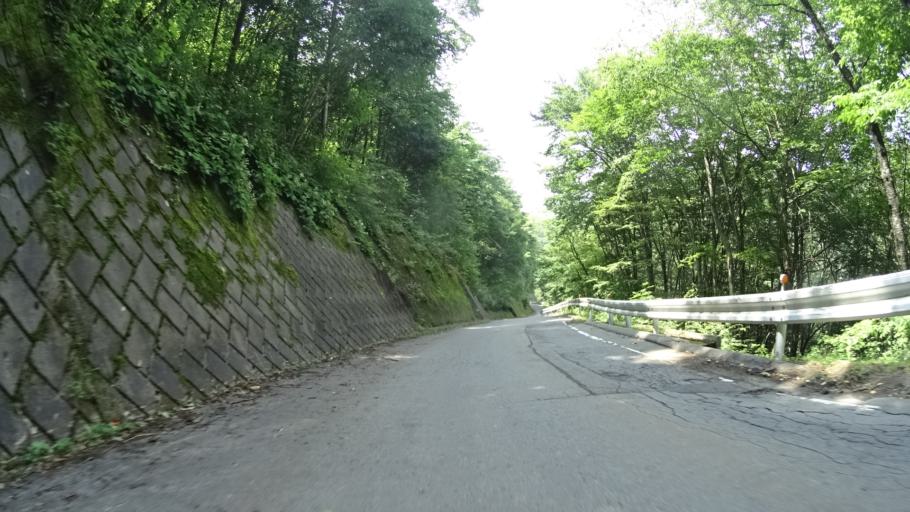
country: JP
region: Nagano
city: Saku
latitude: 36.1025
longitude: 138.6494
